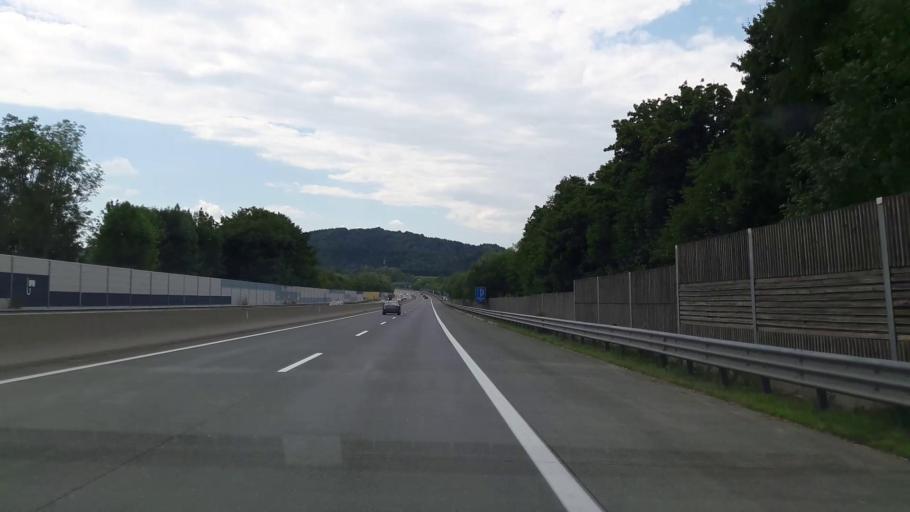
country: AT
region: Upper Austria
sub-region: Politischer Bezirk Vocklabruck
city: Sankt Georgen im Attergau
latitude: 47.9178
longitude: 13.4831
